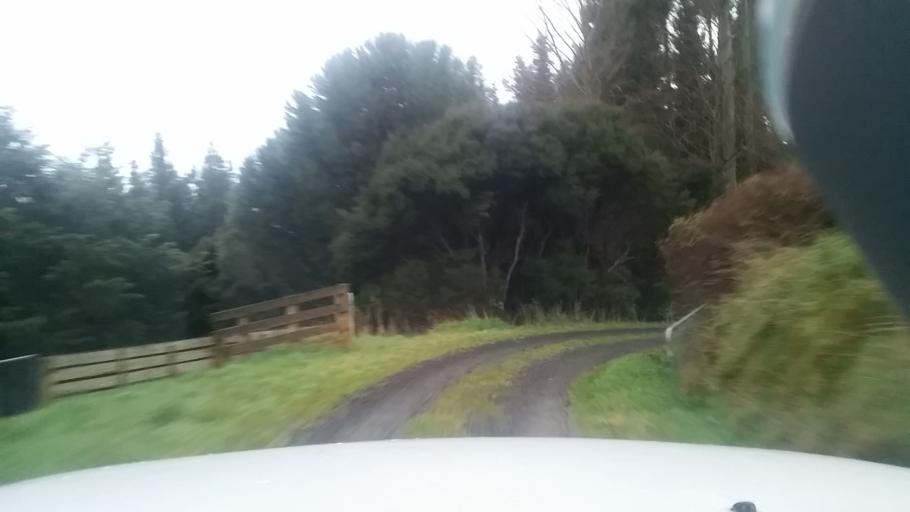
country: NZ
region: Canterbury
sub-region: Christchurch City
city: Christchurch
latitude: -43.7835
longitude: 172.8899
